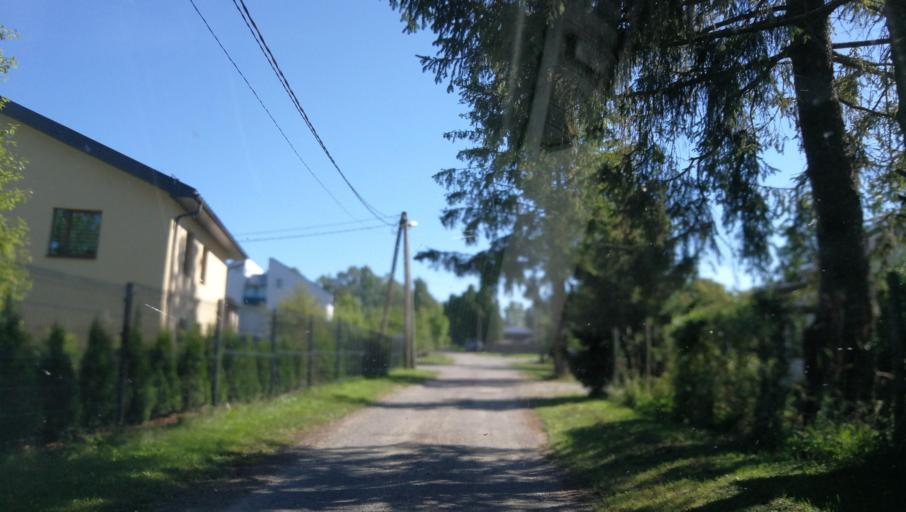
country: LV
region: Cesu Rajons
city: Cesis
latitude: 57.3036
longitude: 25.2488
